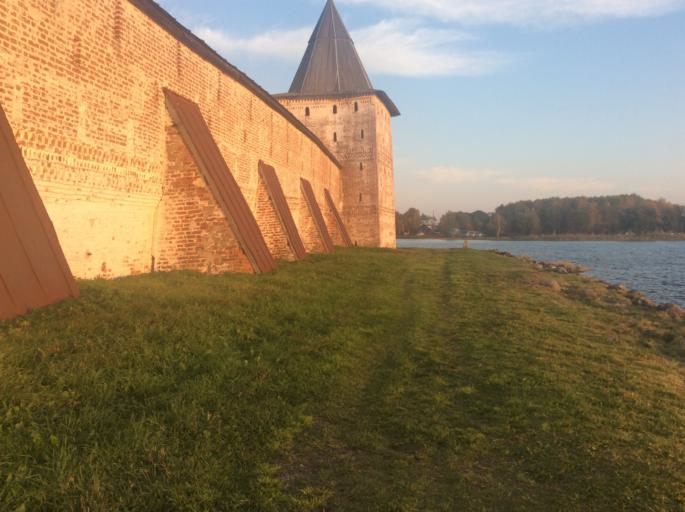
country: RU
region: Vologda
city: Kirillov
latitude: 59.8564
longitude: 38.3662
